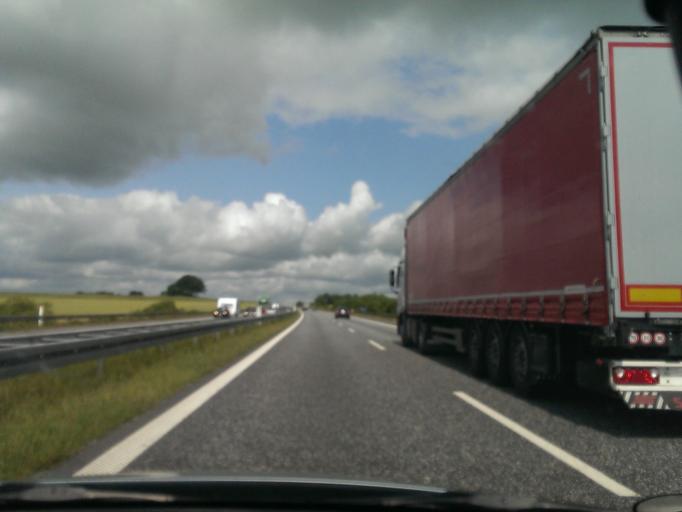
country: DK
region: Central Jutland
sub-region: Randers Kommune
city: Spentrup
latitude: 56.5234
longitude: 9.9494
